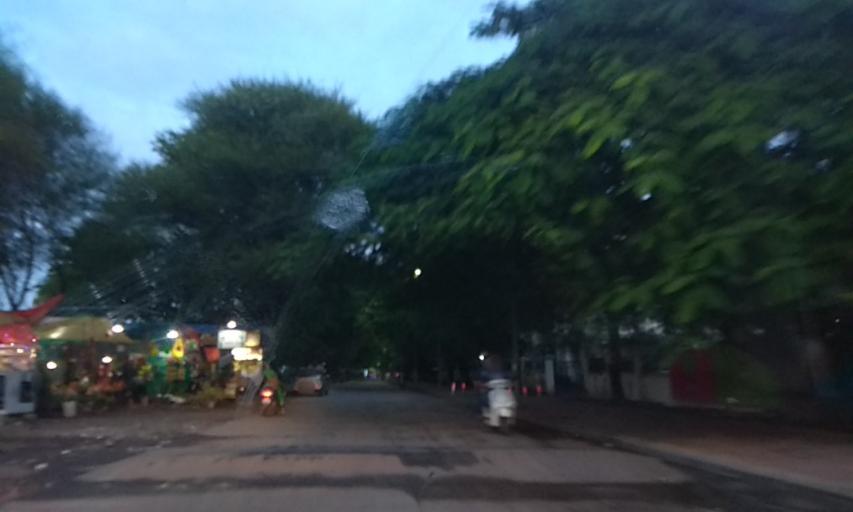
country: IN
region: Maharashtra
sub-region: Pune Division
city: Pune
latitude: 18.5230
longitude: 73.9287
